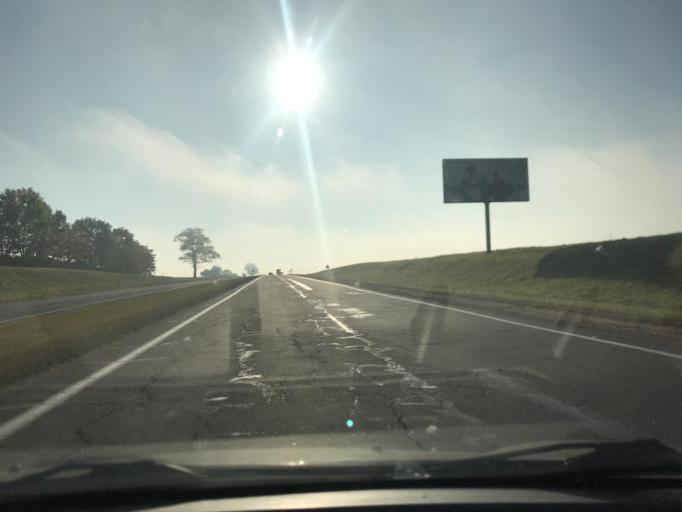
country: BY
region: Minsk
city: Dukora
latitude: 53.6870
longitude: 27.9102
